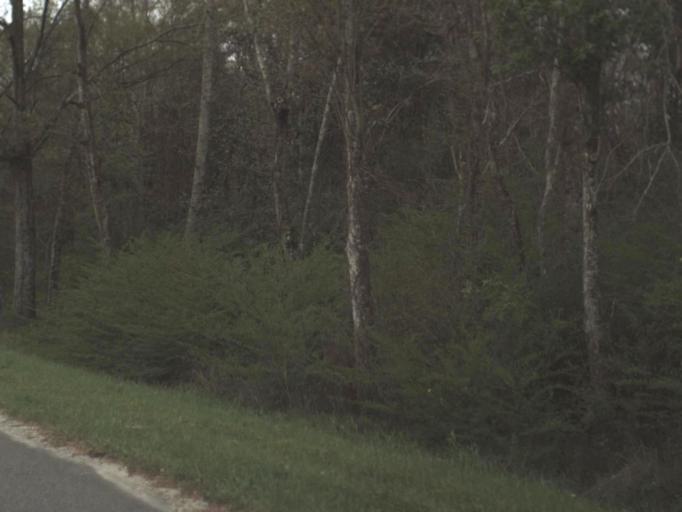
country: US
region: Florida
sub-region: Jackson County
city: Graceville
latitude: 30.9756
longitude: -85.6465
